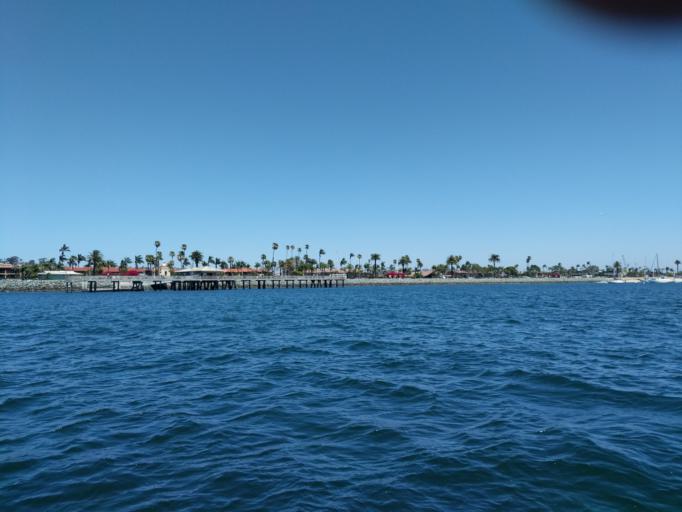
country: US
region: California
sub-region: San Diego County
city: Coronado
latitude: 32.7099
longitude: -117.2275
